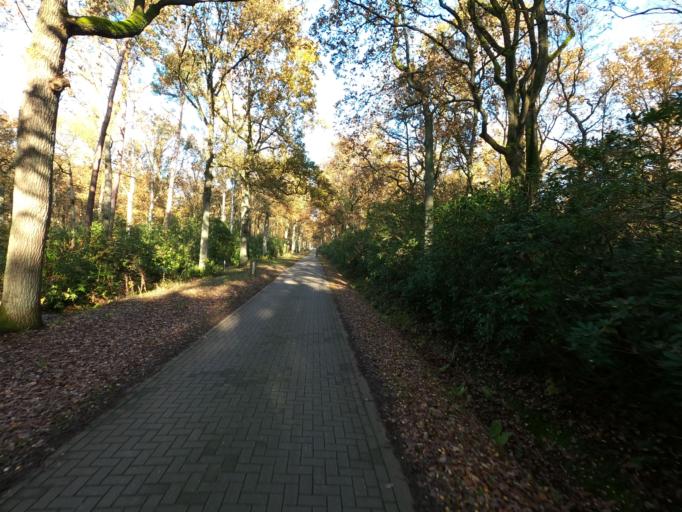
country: BE
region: Flanders
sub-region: Provincie Antwerpen
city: Brasschaat
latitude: 51.3399
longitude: 4.5270
